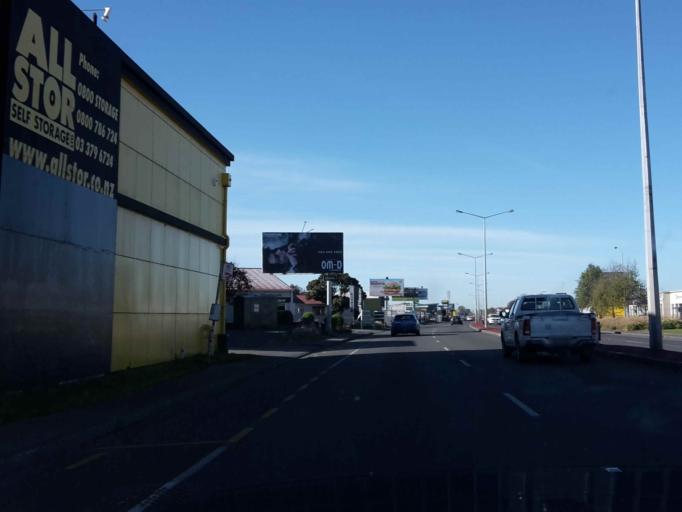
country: NZ
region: Canterbury
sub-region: Selwyn District
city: Prebbleton
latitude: -43.5390
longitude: 172.5585
